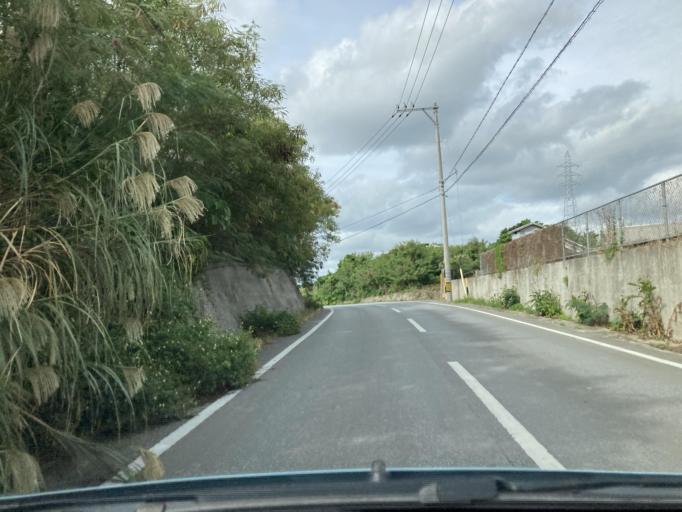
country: JP
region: Okinawa
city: Itoman
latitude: 26.1139
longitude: 127.6886
